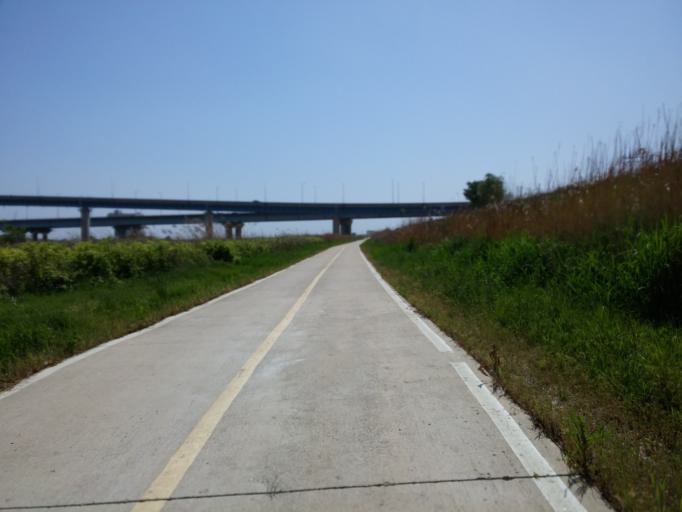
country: KR
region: Chungcheongnam-do
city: Nonsan
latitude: 36.2093
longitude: 127.0771
